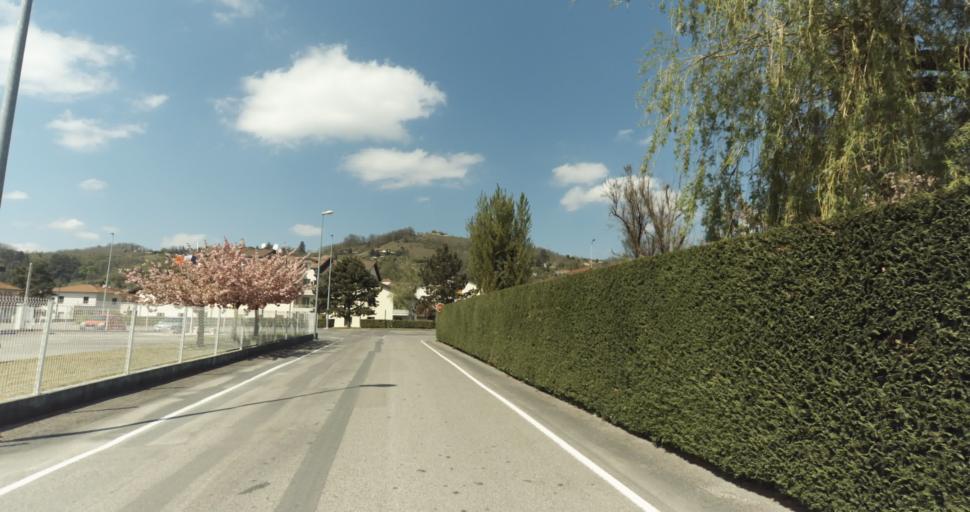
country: FR
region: Rhone-Alpes
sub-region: Departement de l'Isere
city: Saint-Marcellin
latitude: 45.1491
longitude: 5.3105
